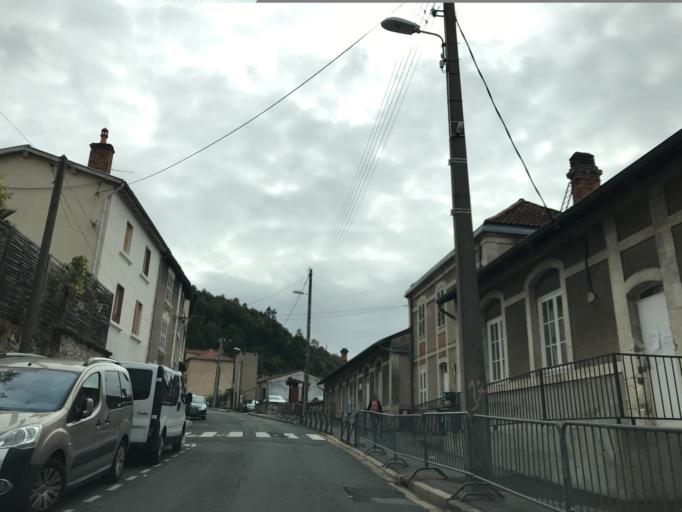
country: FR
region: Auvergne
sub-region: Departement du Puy-de-Dome
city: Thiers
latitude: 45.8531
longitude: 3.5530
